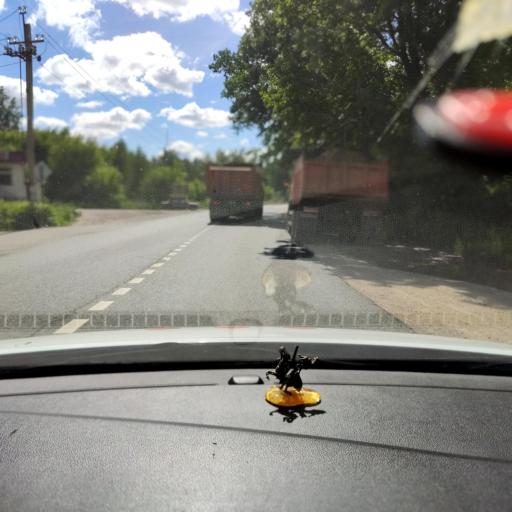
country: RU
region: Tatarstan
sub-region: Zelenodol'skiy Rayon
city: Vasil'yevo
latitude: 55.8454
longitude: 48.6824
